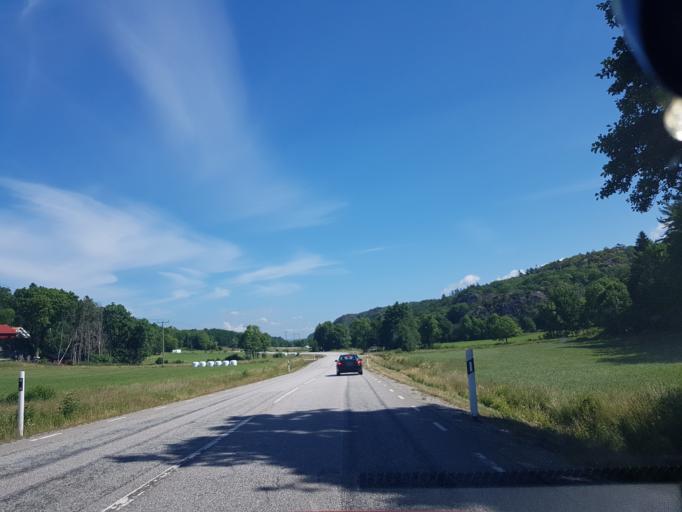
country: SE
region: Vaestra Goetaland
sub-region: Lysekils Kommun
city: Lysekil
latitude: 58.1649
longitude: 11.4795
